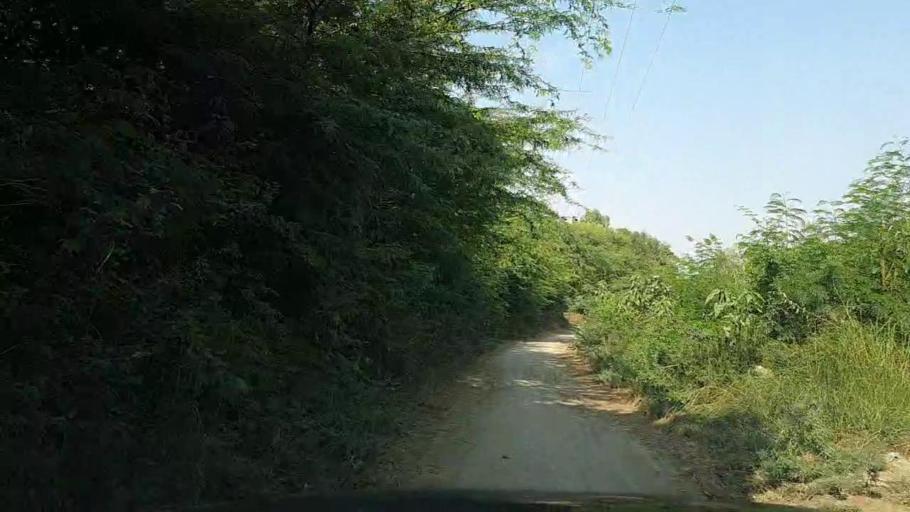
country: PK
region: Sindh
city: Thatta
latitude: 24.7956
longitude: 67.8223
